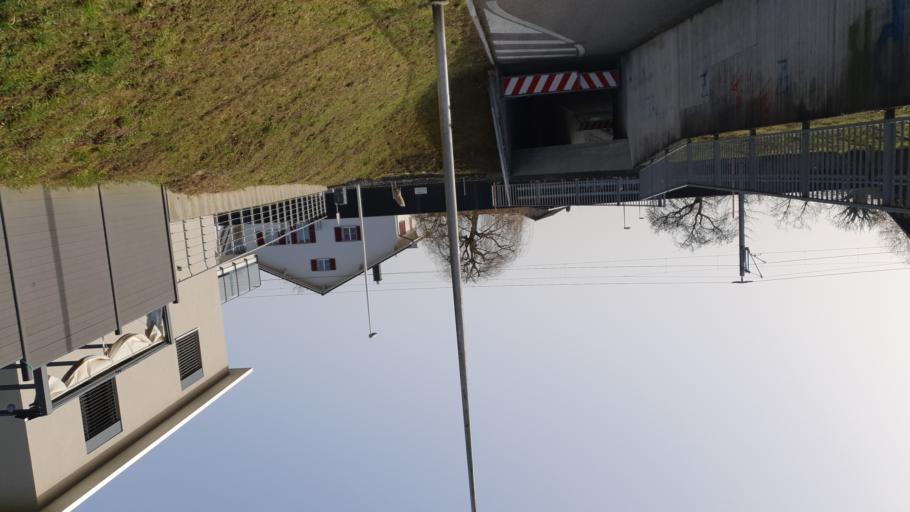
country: CH
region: Solothurn
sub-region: Bezirk Wasseramt
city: Derendingen
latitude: 47.2024
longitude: 7.5865
